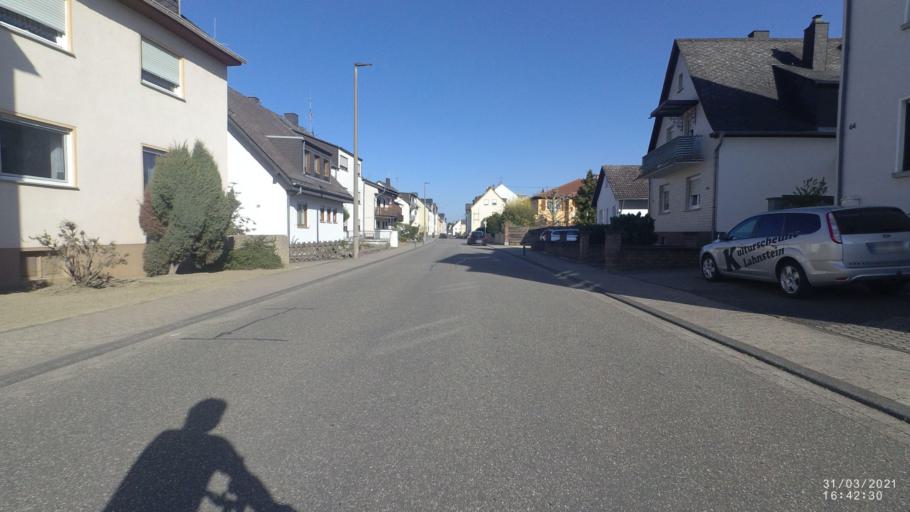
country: DE
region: Rheinland-Pfalz
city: Mulheim-Karlich
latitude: 50.3883
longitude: 7.5079
